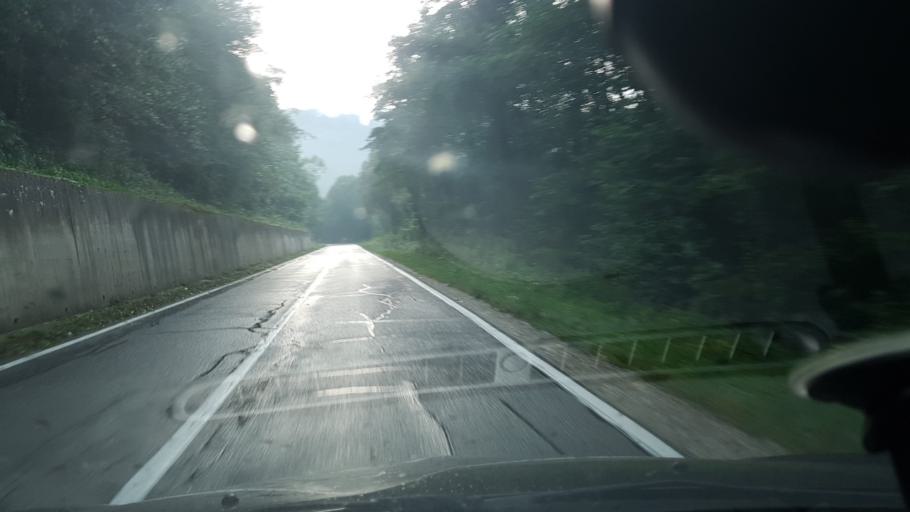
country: SI
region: Rogatec
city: Rogatec
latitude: 46.2210
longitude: 15.7446
